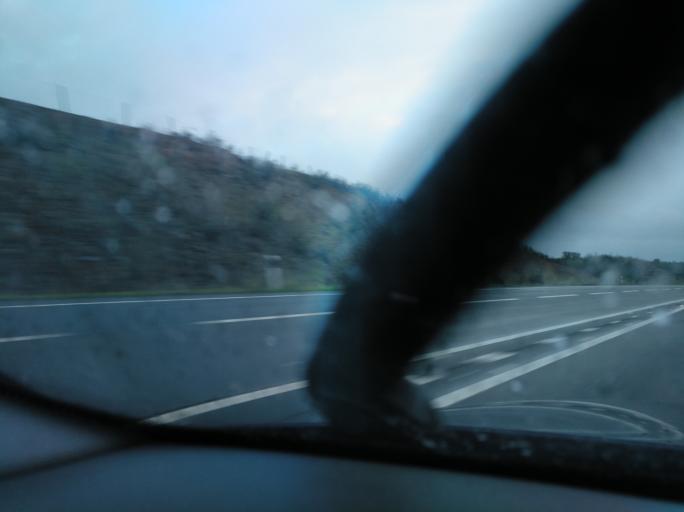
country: PT
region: Faro
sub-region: Castro Marim
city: Castro Marim
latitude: 37.2887
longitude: -7.4864
